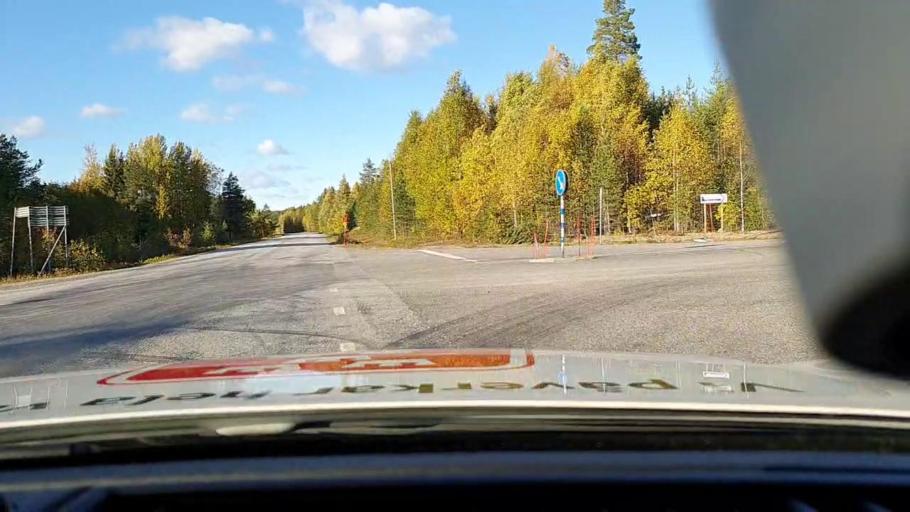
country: SE
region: Norrbotten
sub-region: Pitea Kommun
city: Norrfjarden
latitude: 65.4605
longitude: 21.4531
